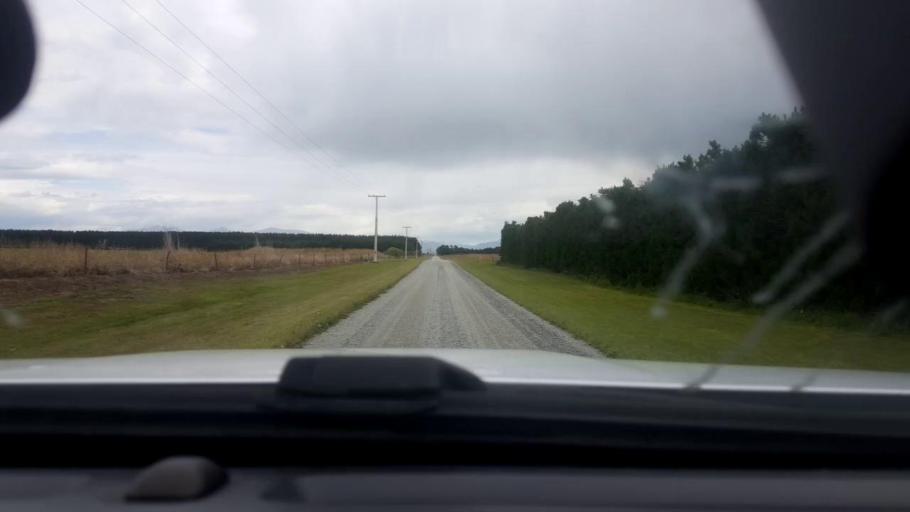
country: NZ
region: Canterbury
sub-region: Timaru District
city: Timaru
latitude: -44.1657
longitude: 171.4095
